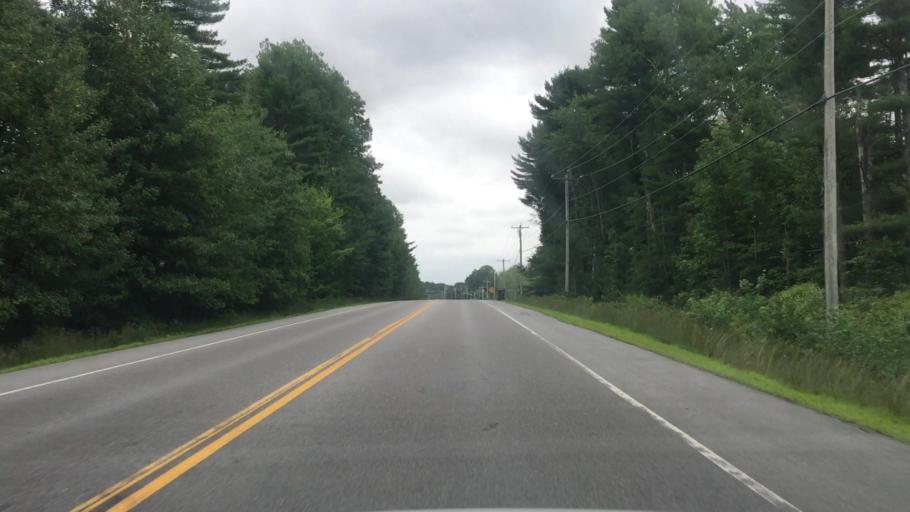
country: US
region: Maine
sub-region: York County
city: Dayton
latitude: 43.5354
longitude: -70.5098
